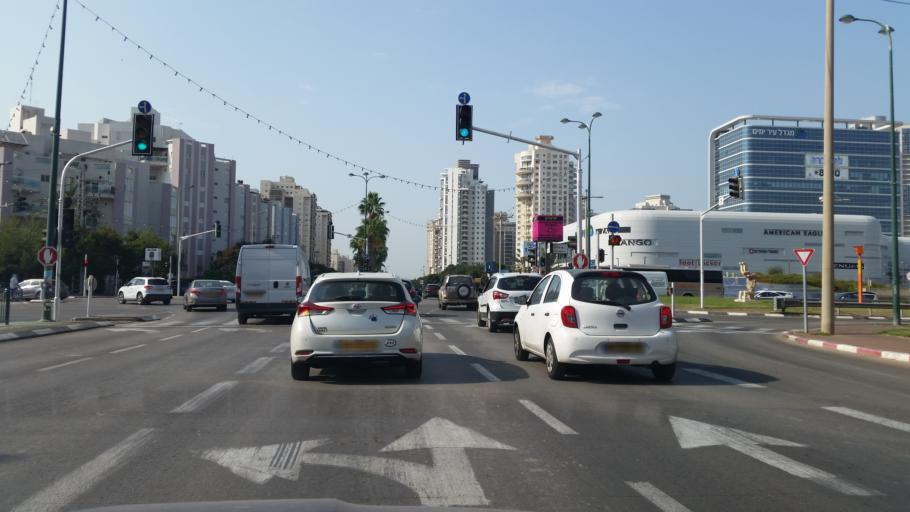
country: IL
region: Central District
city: Even Yehuda
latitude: 32.2783
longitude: 34.8501
